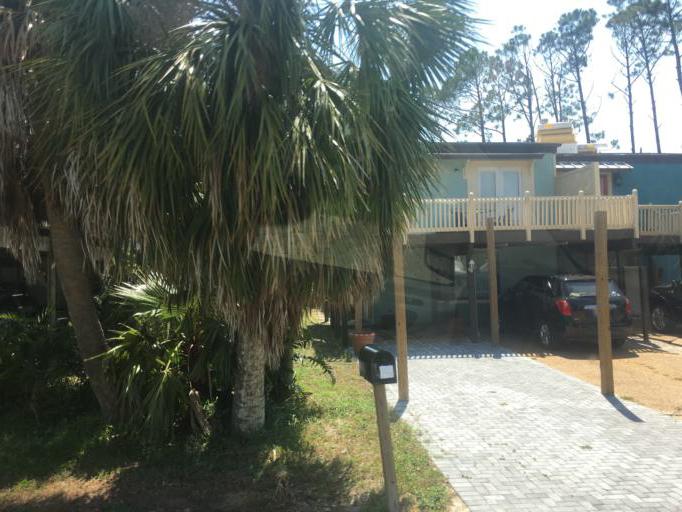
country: US
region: Florida
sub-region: Bay County
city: Lower Grand Lagoon
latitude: 30.1605
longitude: -85.7727
